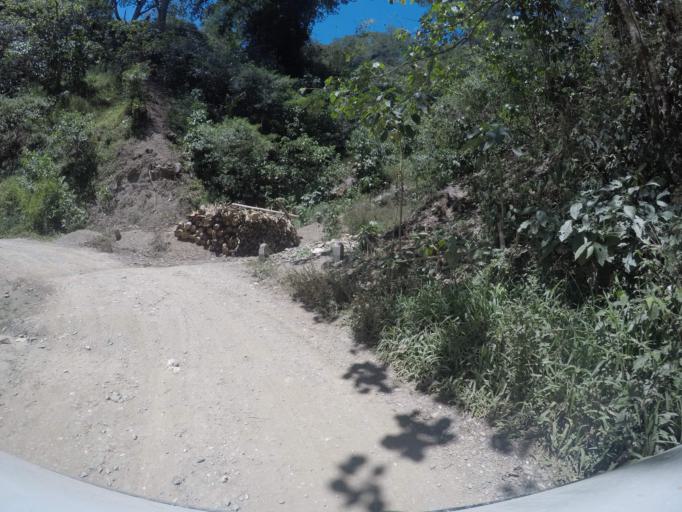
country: TL
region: Ermera
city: Gleno
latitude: -8.7413
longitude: 125.4063
